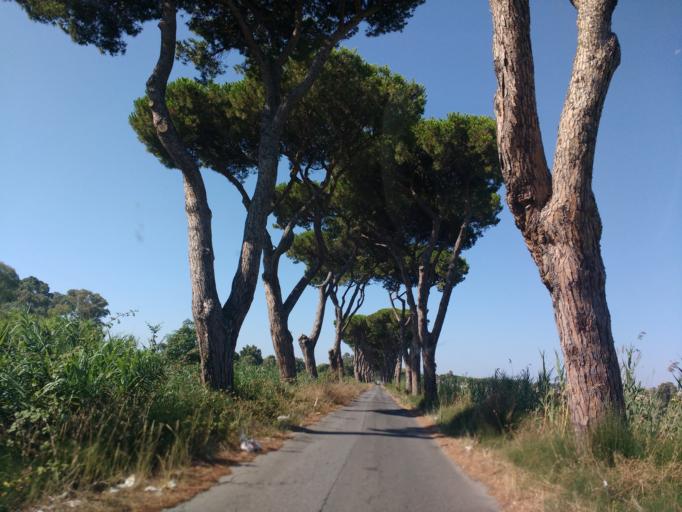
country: IT
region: Latium
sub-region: Citta metropolitana di Roma Capitale
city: Acilia-Castel Fusano-Ostia Antica
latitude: 41.7496
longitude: 12.3265
